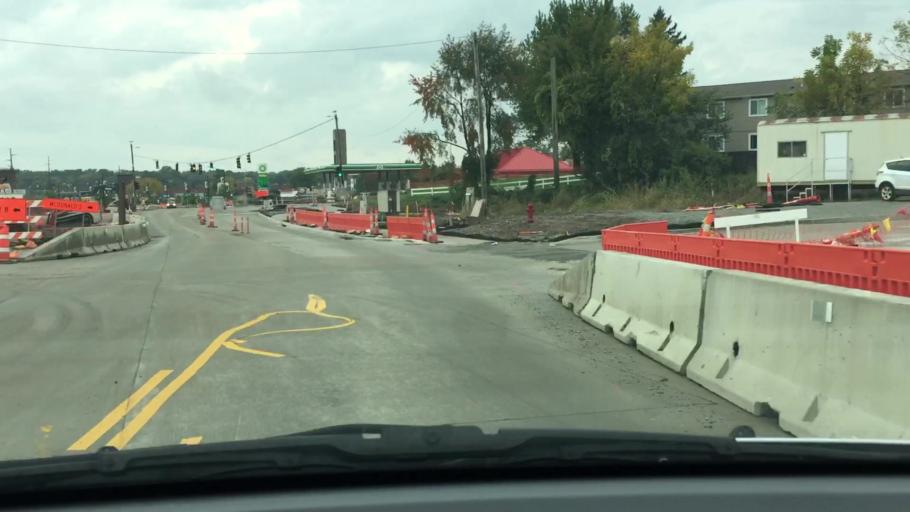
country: US
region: Iowa
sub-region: Johnson County
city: Coralville
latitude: 41.6777
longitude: -91.5660
